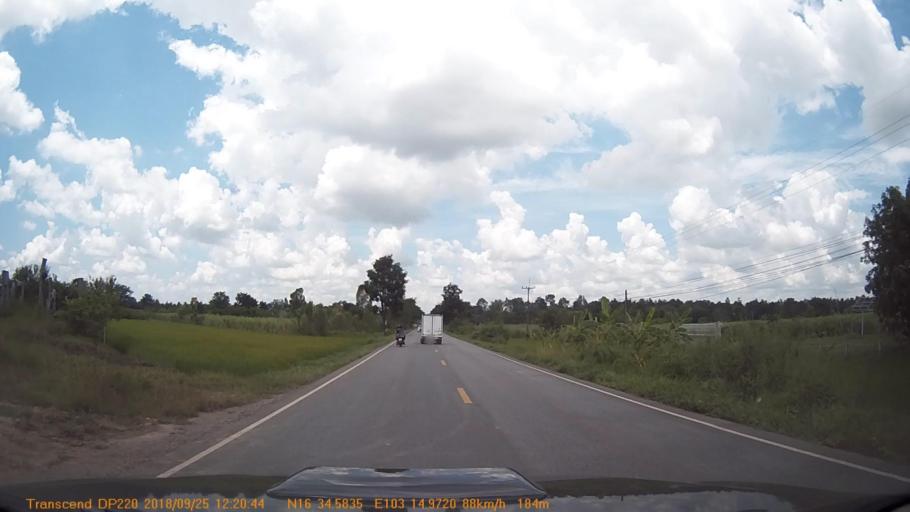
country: TH
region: Kalasin
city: Huai Mek
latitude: 16.5765
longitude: 103.2494
